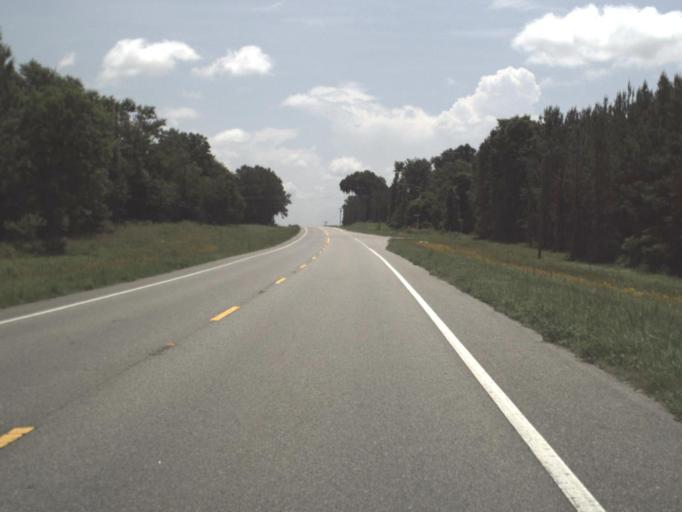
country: US
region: Florida
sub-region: Madison County
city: Madison
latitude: 30.4883
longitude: -83.4957
